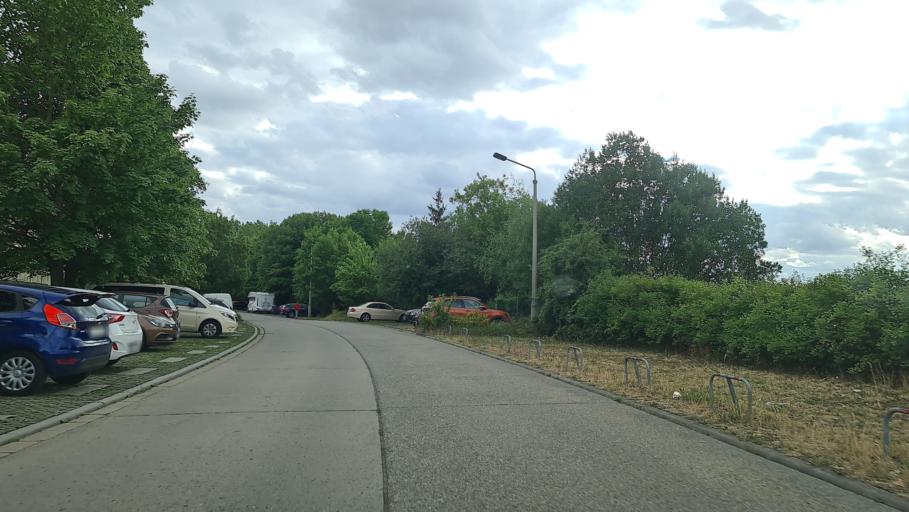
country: DE
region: Saxony
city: Plauen
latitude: 50.4997
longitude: 12.1610
